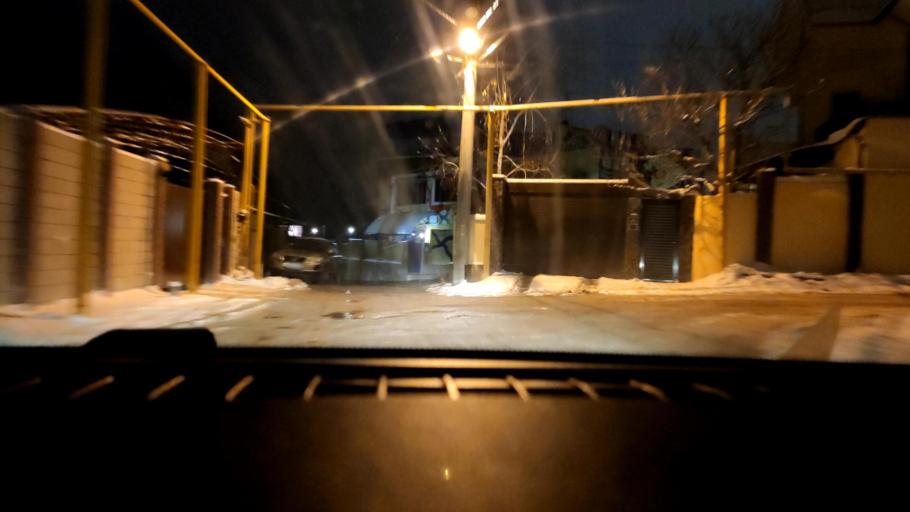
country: RU
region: Samara
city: Samara
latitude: 53.2414
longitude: 50.1692
